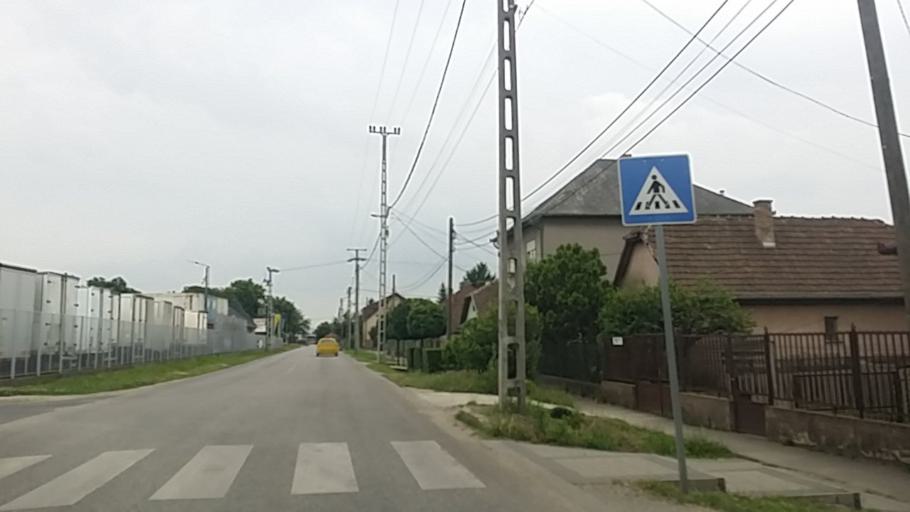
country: HU
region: Pest
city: Vecses
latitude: 47.4088
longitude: 19.2542
